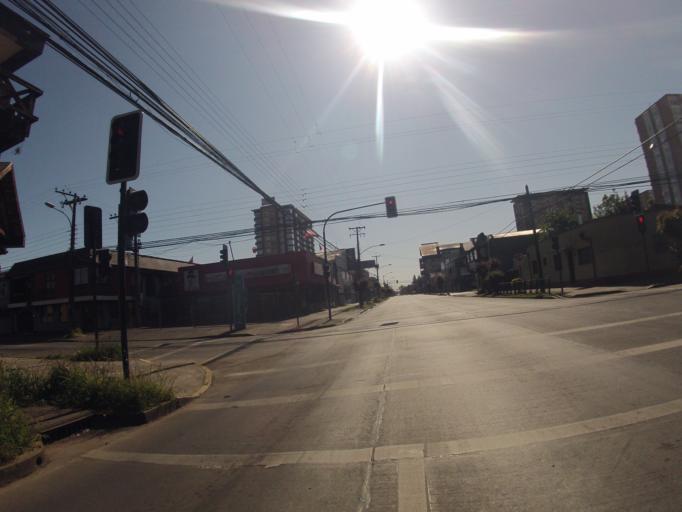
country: CL
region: Araucania
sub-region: Provincia de Cautin
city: Temuco
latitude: -38.7425
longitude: -72.5942
